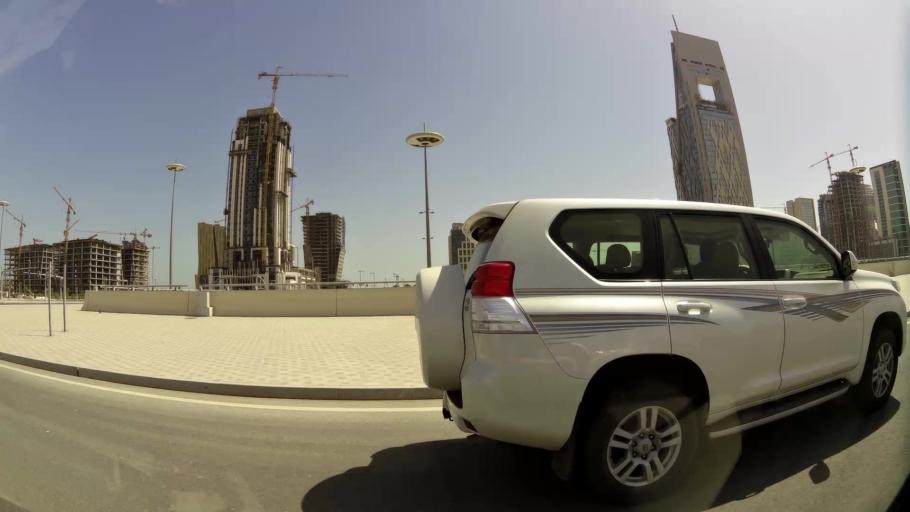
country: QA
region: Baladiyat ad Dawhah
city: Doha
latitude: 25.3926
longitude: 51.5166
